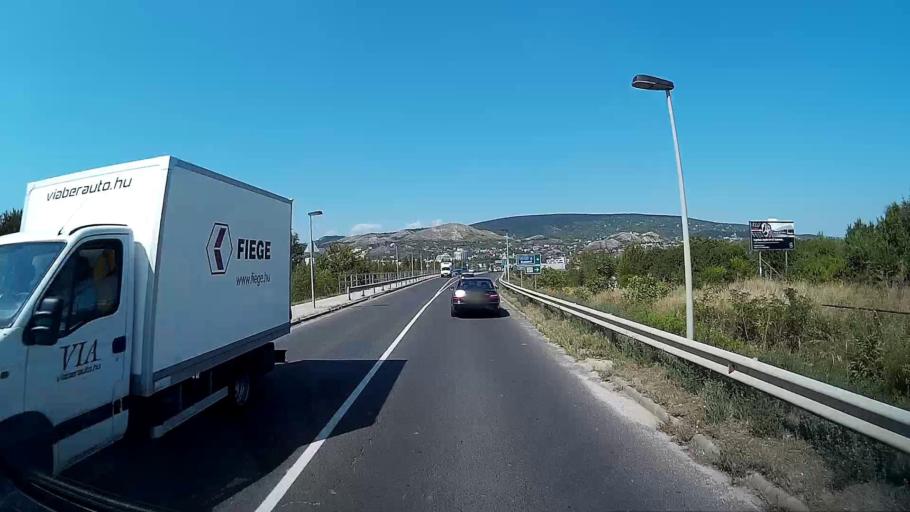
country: HU
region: Pest
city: Budaors
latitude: 47.4488
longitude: 18.9479
